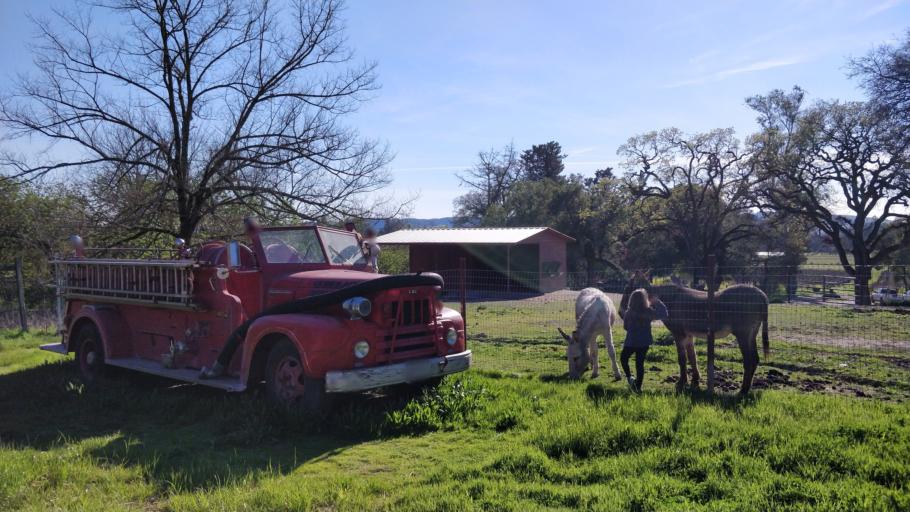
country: US
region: California
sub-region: Sonoma County
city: Sonoma
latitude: 38.2781
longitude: -122.4159
